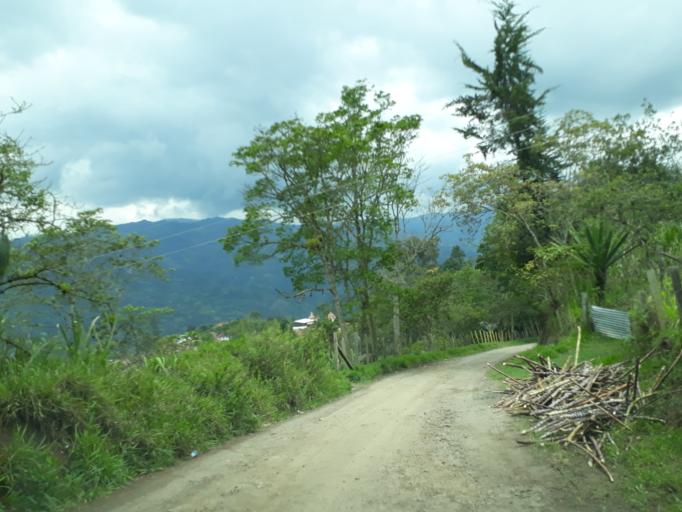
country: CO
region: Cundinamarca
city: Manta
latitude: 5.0134
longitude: -73.5406
